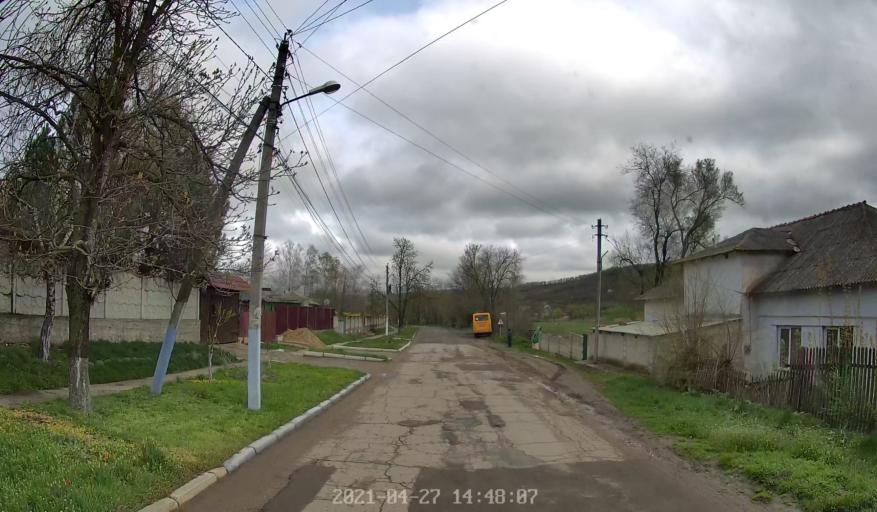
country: MD
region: Chisinau
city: Vadul lui Voda
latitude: 47.0514
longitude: 29.0395
